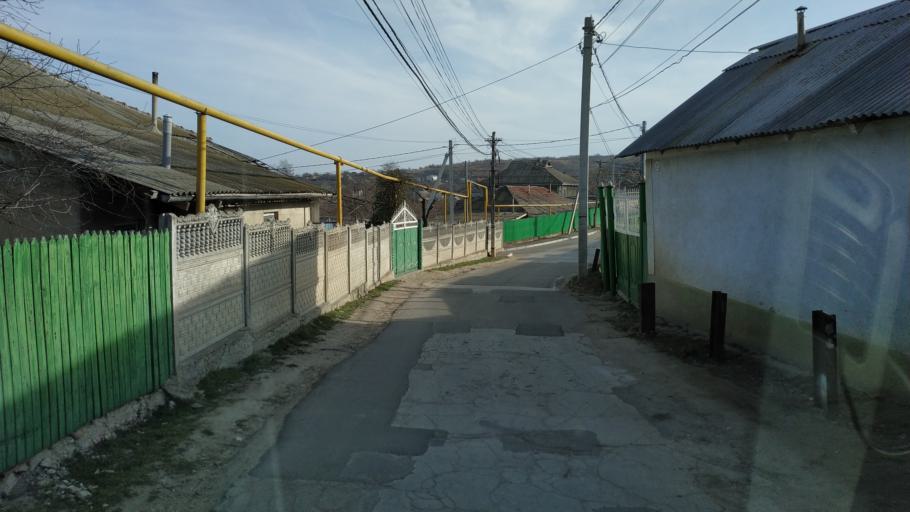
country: MD
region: Chisinau
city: Vatra
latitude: 47.0699
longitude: 28.6740
